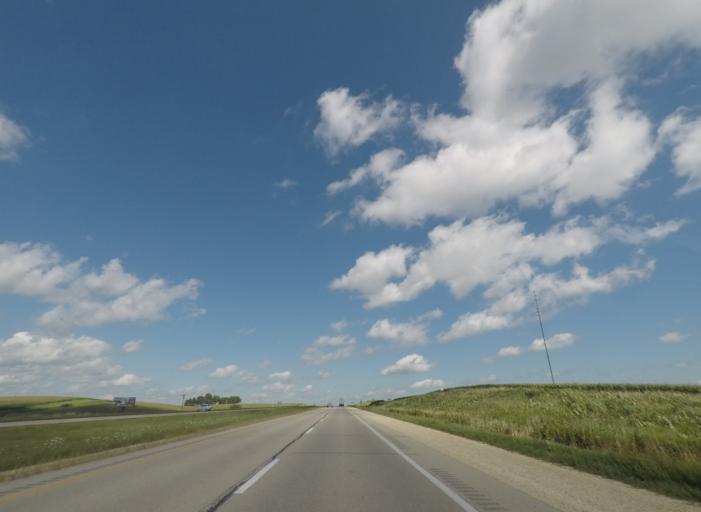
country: US
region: Iowa
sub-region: Dubuque County
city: Cascade
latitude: 42.3117
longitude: -90.9825
